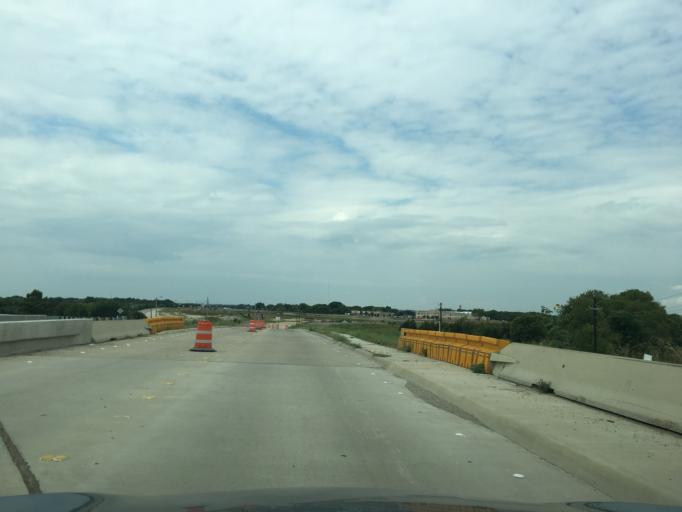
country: US
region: Texas
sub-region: Collin County
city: Melissa
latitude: 33.2747
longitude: -96.5764
